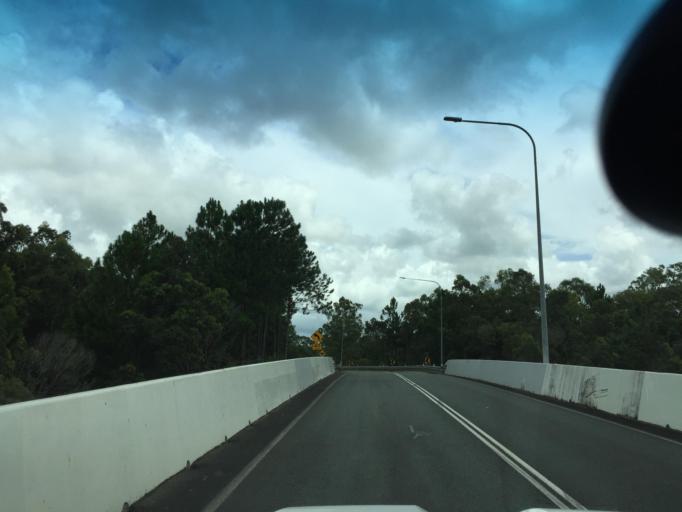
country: AU
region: Queensland
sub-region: Moreton Bay
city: Caboolture
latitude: -27.0608
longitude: 152.9088
